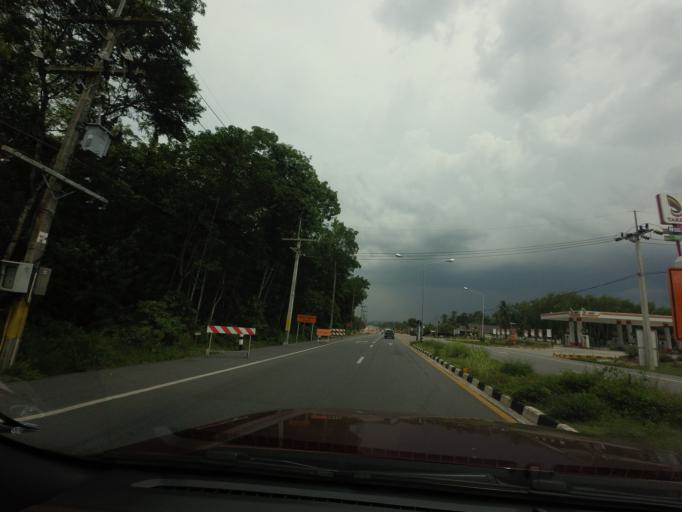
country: TH
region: Yala
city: Krong Pi Nang
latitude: 6.4543
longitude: 101.2747
